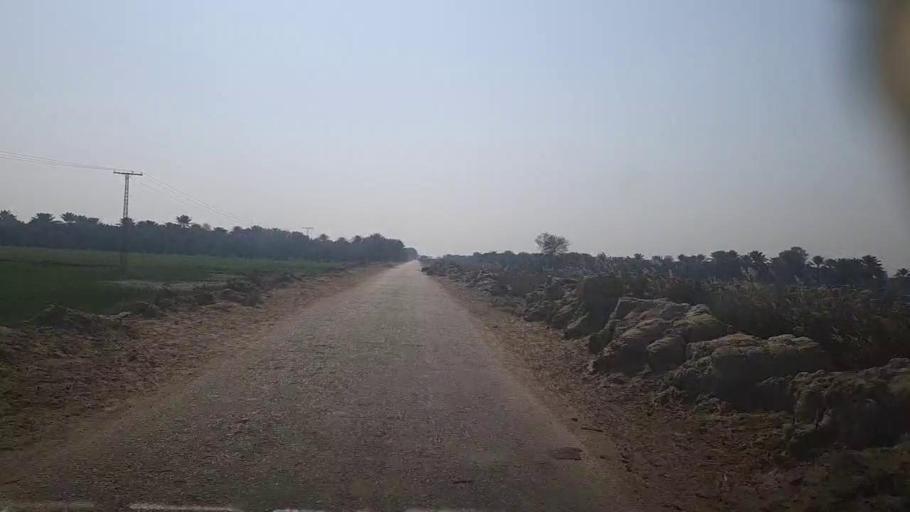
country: PK
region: Sindh
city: Khairpur
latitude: 27.4563
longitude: 68.8144
